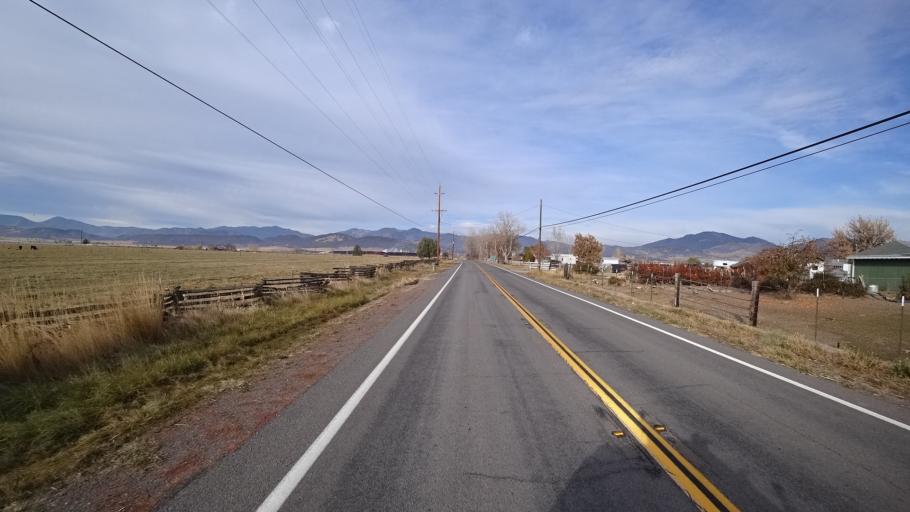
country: US
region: California
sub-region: Siskiyou County
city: Montague
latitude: 41.7306
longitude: -122.5760
